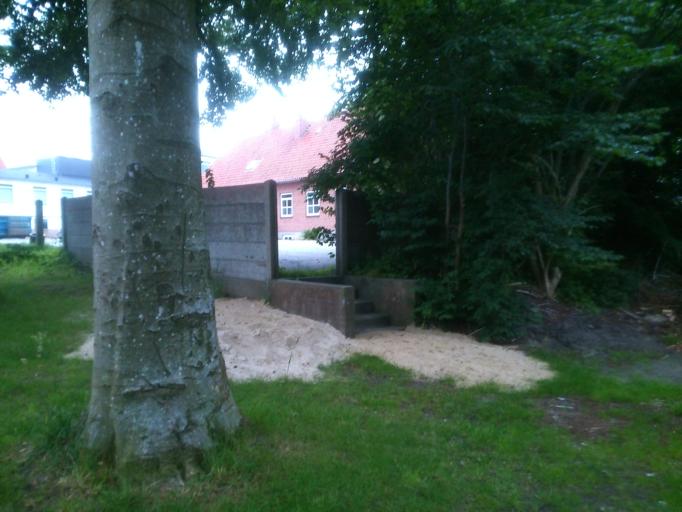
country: DK
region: Central Jutland
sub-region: Ringkobing-Skjern Kommune
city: Tarm
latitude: 55.9054
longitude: 8.5220
